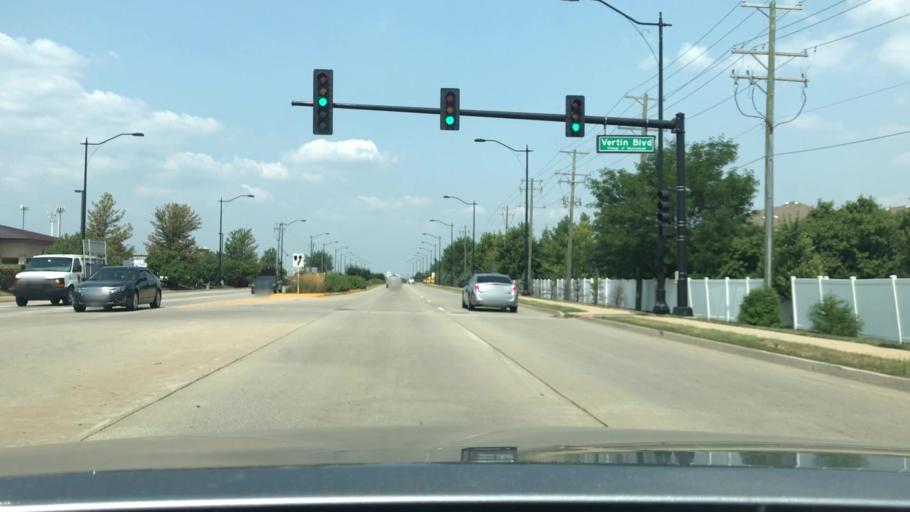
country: US
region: Illinois
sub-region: Will County
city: Shorewood
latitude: 41.5406
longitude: -88.1993
